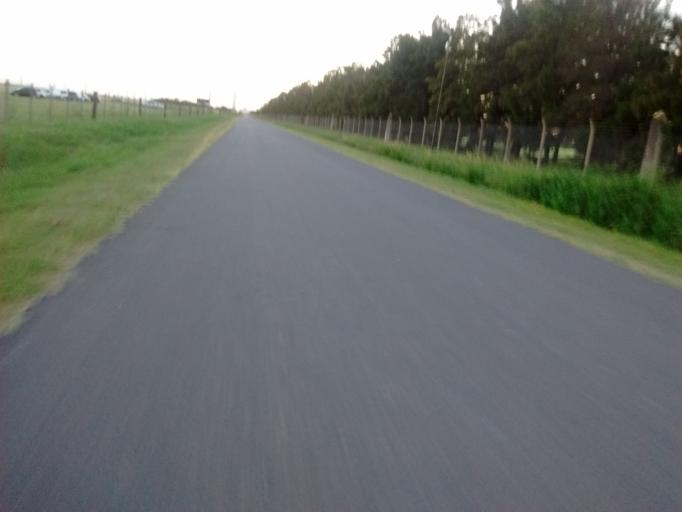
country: AR
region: Santa Fe
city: Funes
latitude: -32.9485
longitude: -60.8195
